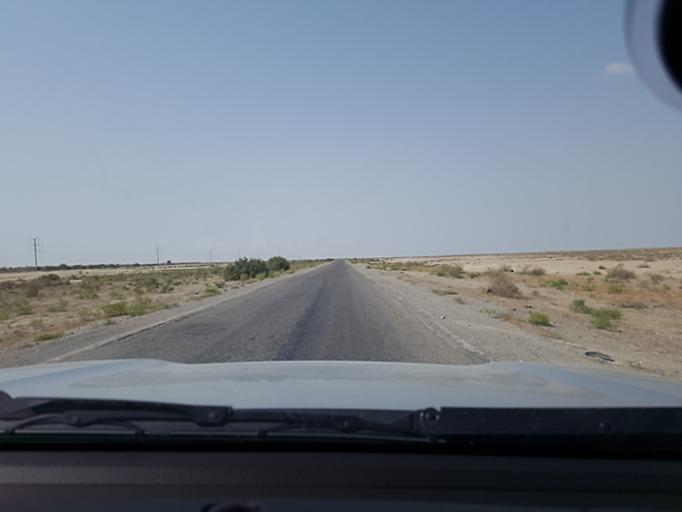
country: TM
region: Balkan
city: Gumdag
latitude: 38.7841
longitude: 54.5946
